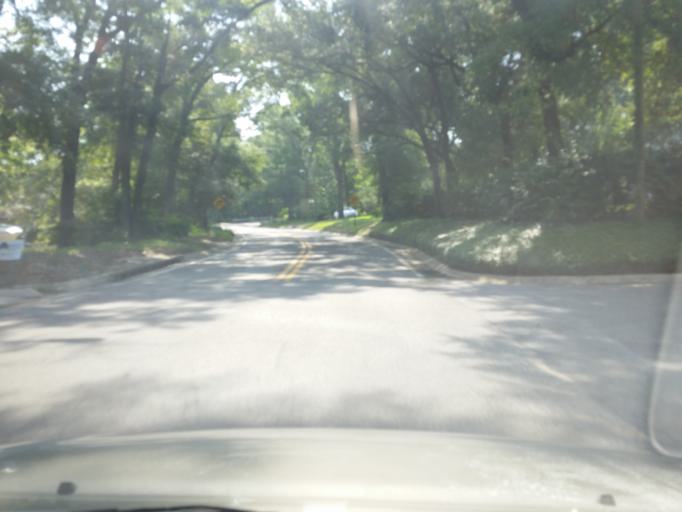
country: US
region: Florida
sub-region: Escambia County
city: Goulding
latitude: 30.4500
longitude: -87.2025
